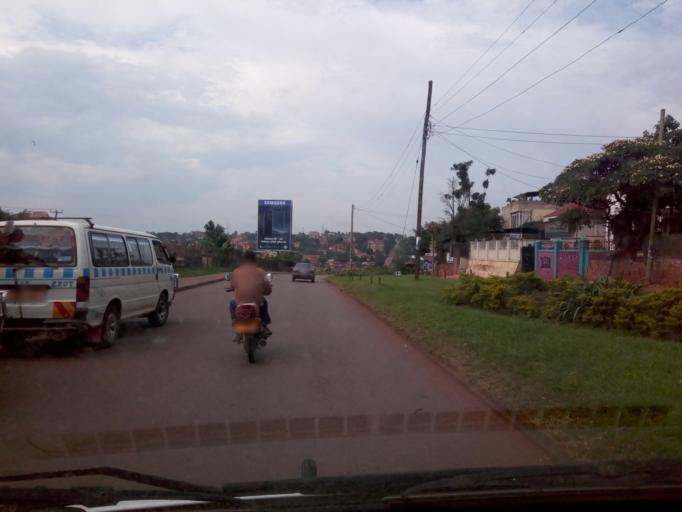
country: UG
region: Central Region
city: Kampala Central Division
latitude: 0.3423
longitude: 32.5896
